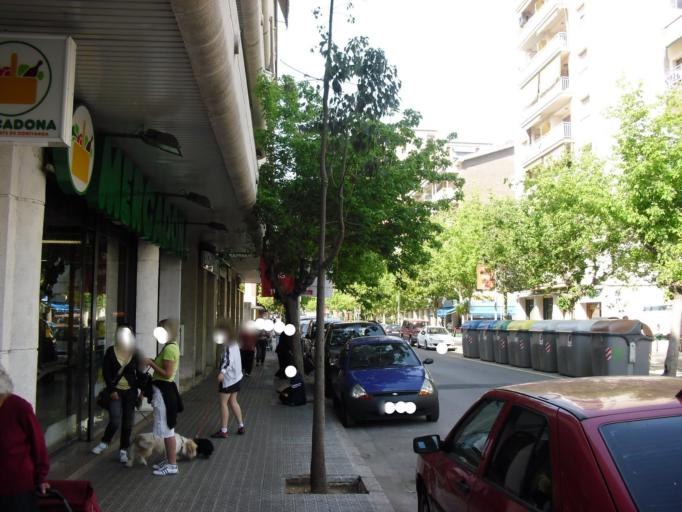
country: ES
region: Catalonia
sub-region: Provincia de Barcelona
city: Vilanova i la Geltru
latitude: 41.2209
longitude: 1.7159
